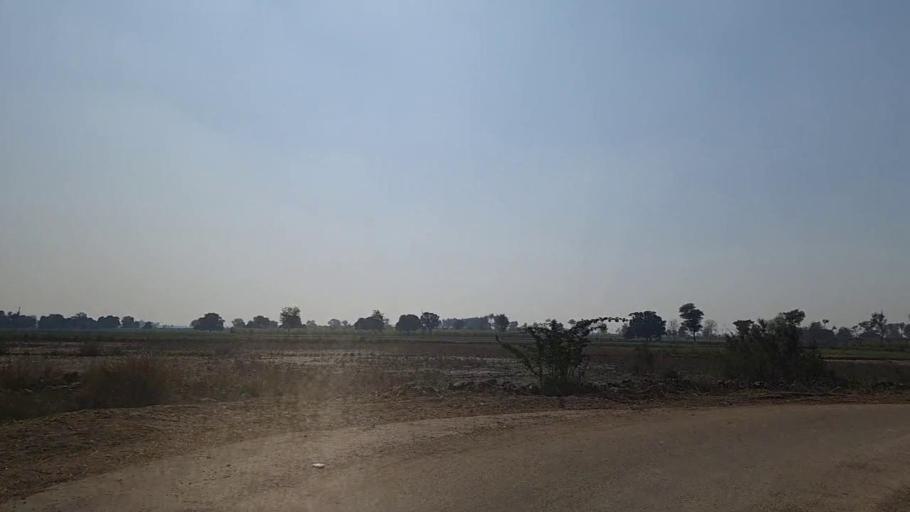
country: PK
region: Sindh
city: Daur
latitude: 26.5026
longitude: 68.3144
